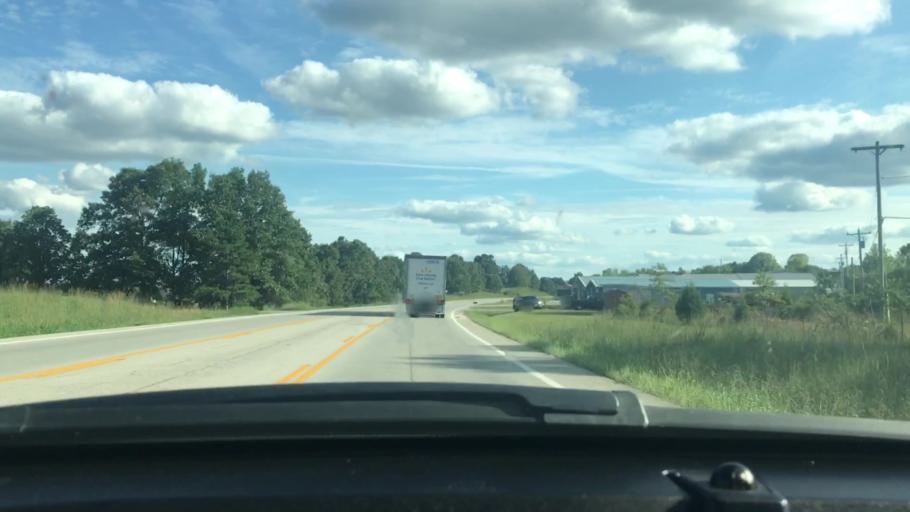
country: US
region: Missouri
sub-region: Oregon County
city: Thayer
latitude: 36.6051
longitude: -91.6446
